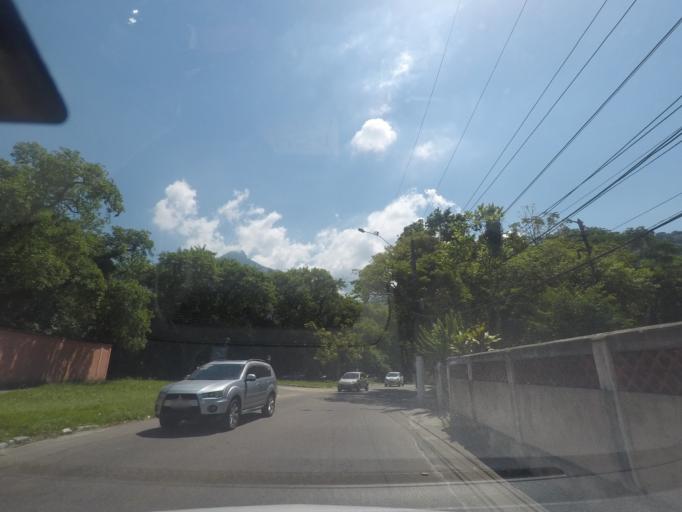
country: BR
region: Rio de Janeiro
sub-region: Petropolis
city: Petropolis
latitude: -22.5764
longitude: -43.1864
